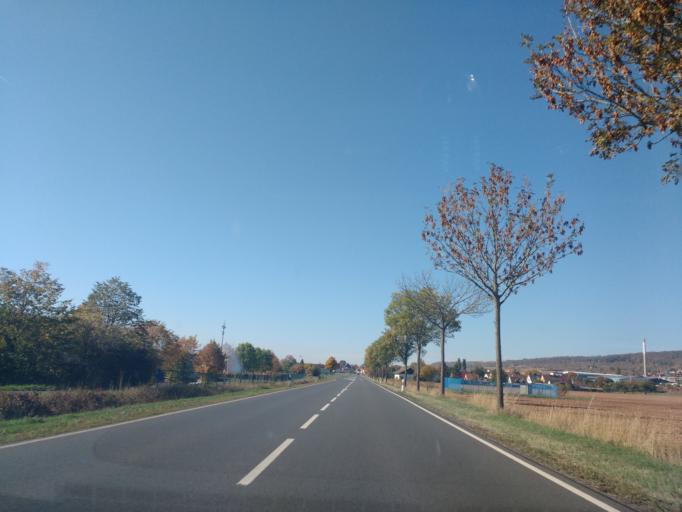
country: DE
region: Saxony-Anhalt
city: Wallhausen
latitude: 51.4603
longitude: 11.2198
